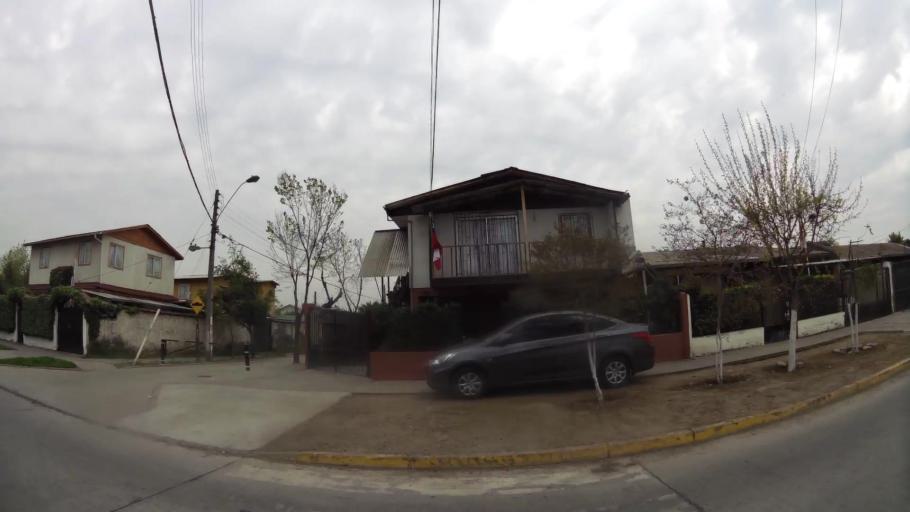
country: CL
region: Santiago Metropolitan
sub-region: Provincia de Santiago
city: Villa Presidente Frei, Nunoa, Santiago, Chile
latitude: -33.5071
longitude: -70.5969
